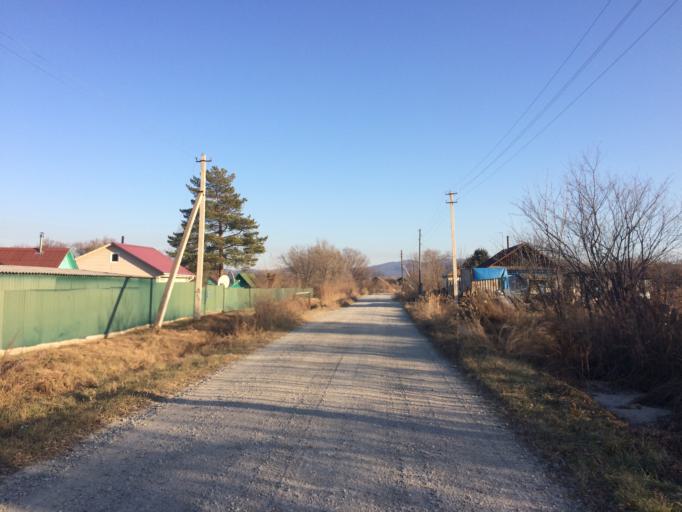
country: RU
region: Primorskiy
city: Ivanovka
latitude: 43.9561
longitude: 132.4815
